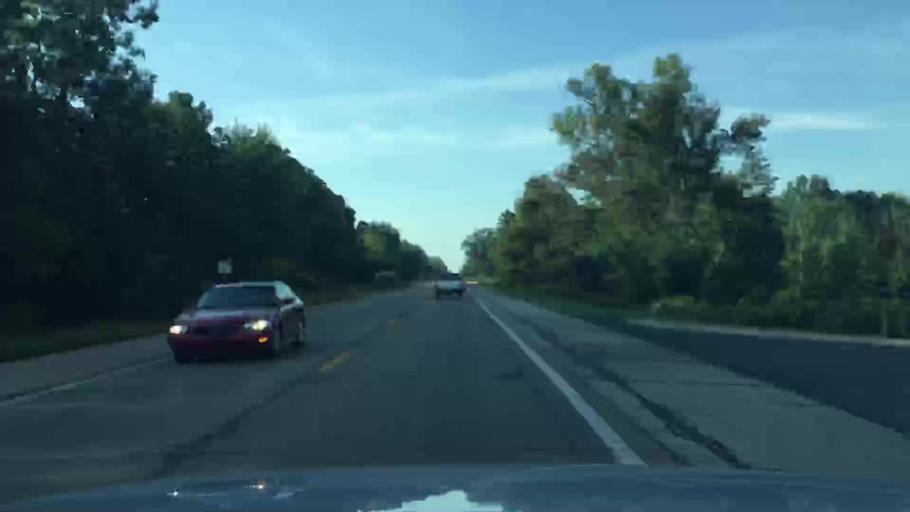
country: US
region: Michigan
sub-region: Jackson County
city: Vandercook Lake
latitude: 42.1136
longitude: -84.3641
